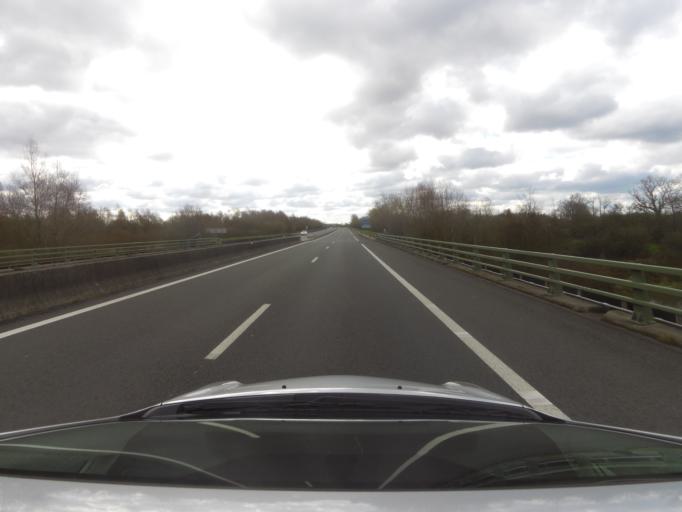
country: FR
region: Picardie
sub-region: Departement de la Somme
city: Quend
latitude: 50.3433
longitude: 1.6933
